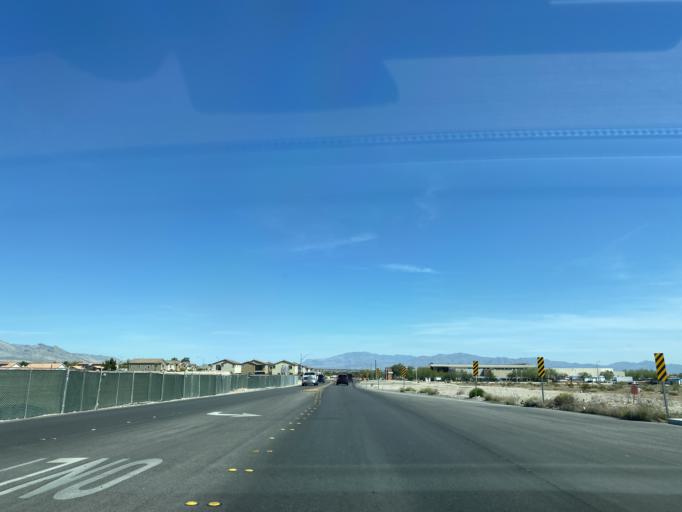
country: US
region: Nevada
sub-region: Clark County
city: Spring Valley
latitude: 36.0755
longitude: -115.2607
